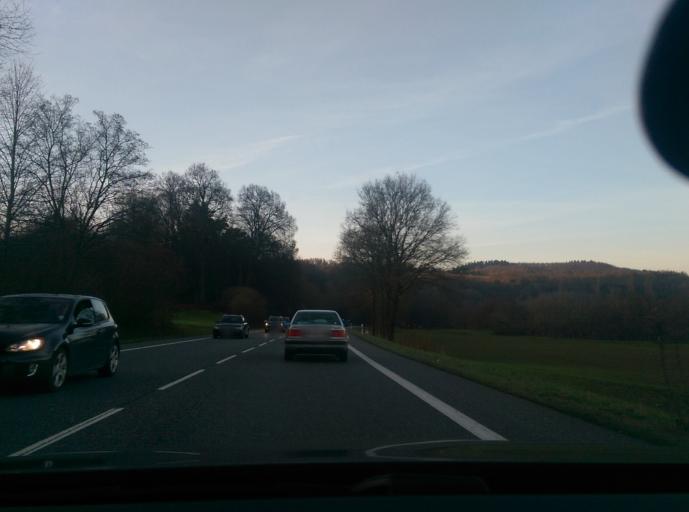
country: DE
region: Hesse
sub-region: Regierungsbezirk Kassel
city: Bad Sooden-Allendorf
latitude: 51.2152
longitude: 9.9871
